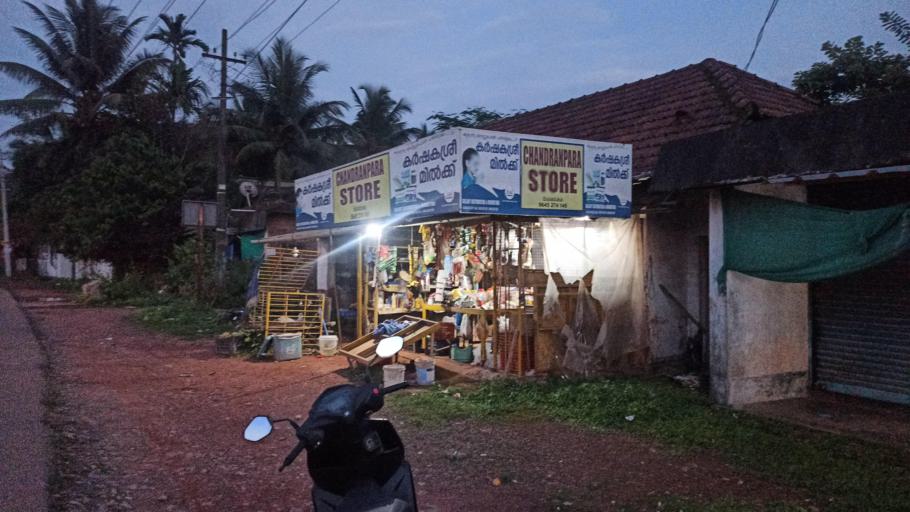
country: IN
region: Kerala
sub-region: Kasaragod District
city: Kasaragod
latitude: 12.5417
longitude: 75.0872
